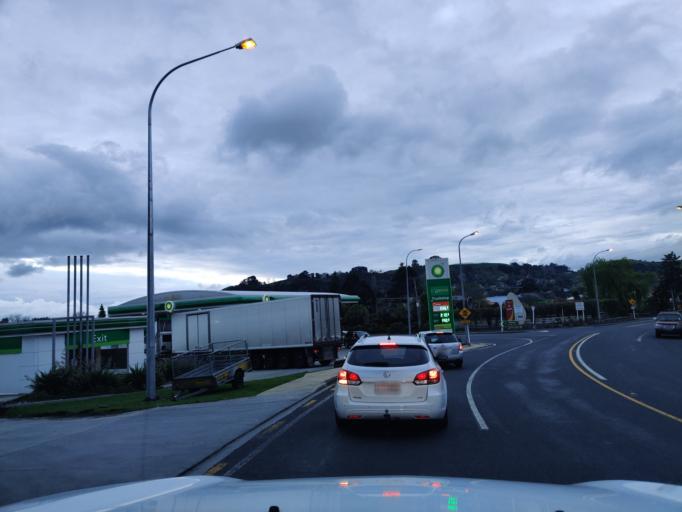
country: NZ
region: Waikato
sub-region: Otorohanga District
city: Otorohanga
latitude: -38.3386
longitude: 175.1670
